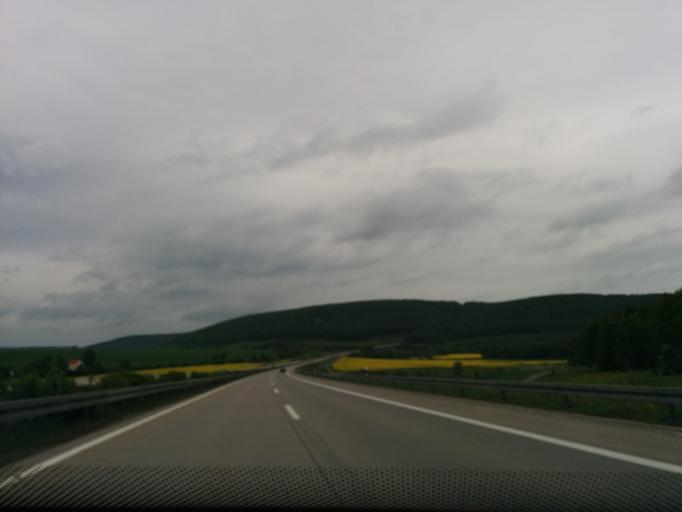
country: DE
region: Thuringia
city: Wolfershausen
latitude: 50.4924
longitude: 10.4412
